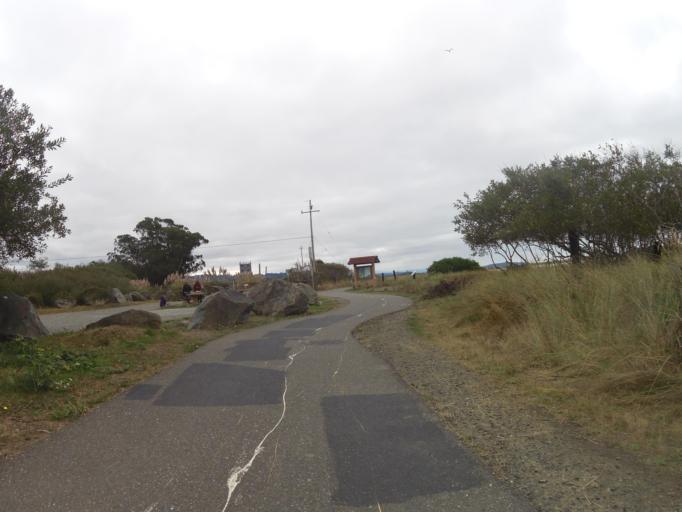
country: US
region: California
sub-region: Humboldt County
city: Bayview
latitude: 40.7729
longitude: -124.1951
